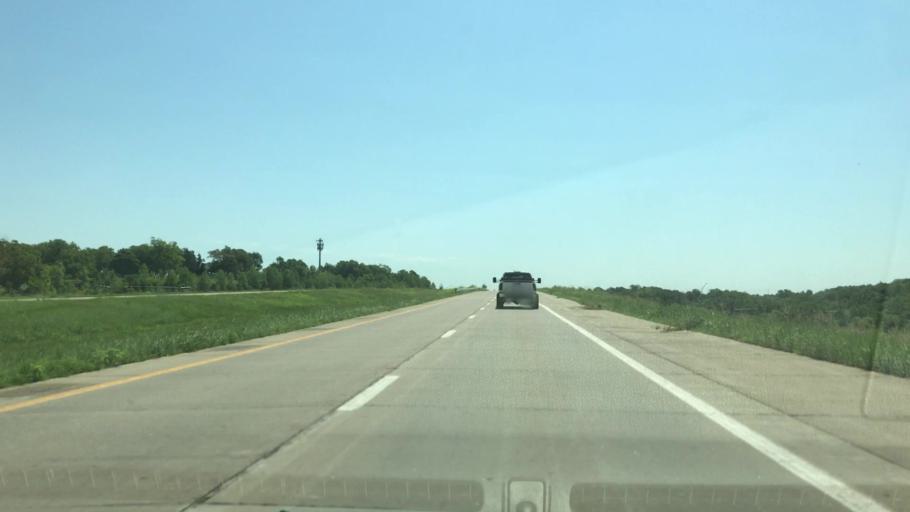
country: US
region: Missouri
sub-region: Jackson County
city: Grandview
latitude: 38.8626
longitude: -94.5887
